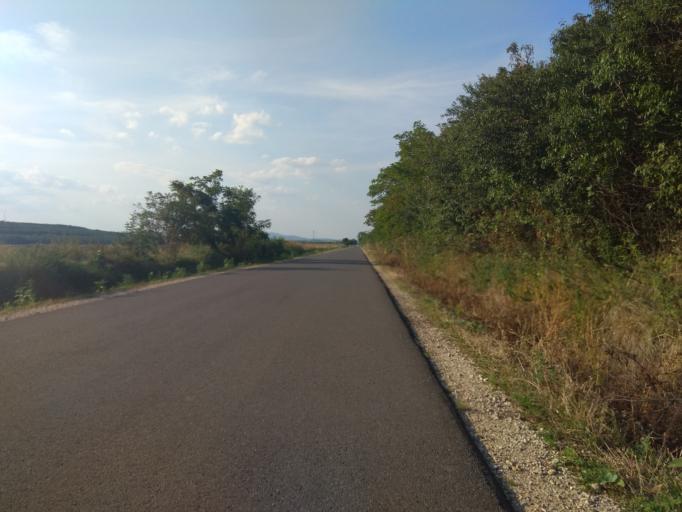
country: HU
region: Borsod-Abauj-Zemplen
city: Harsany
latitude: 47.9040
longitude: 20.7442
